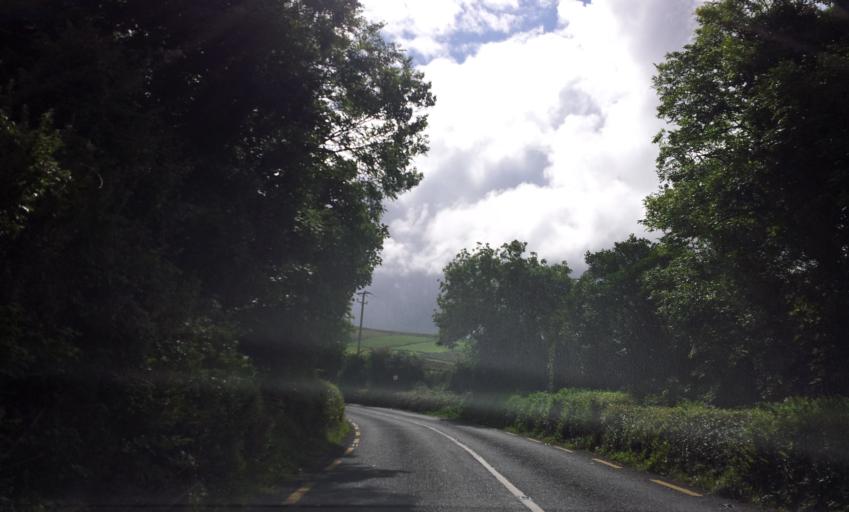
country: IE
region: Munster
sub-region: Ciarrai
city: Killorglin
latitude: 52.2248
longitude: -9.9007
